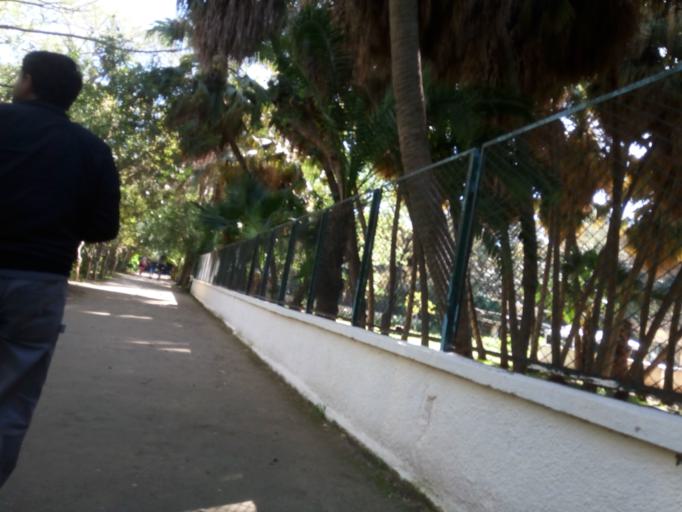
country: DZ
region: Alger
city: Algiers
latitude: 36.7484
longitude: 3.0784
